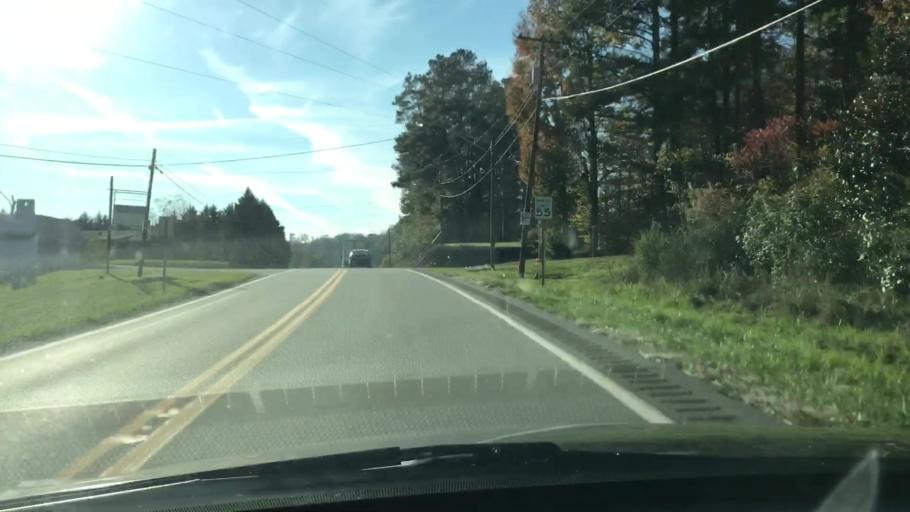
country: US
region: Alabama
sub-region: Cleburne County
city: Heflin
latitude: 33.6408
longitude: -85.6031
